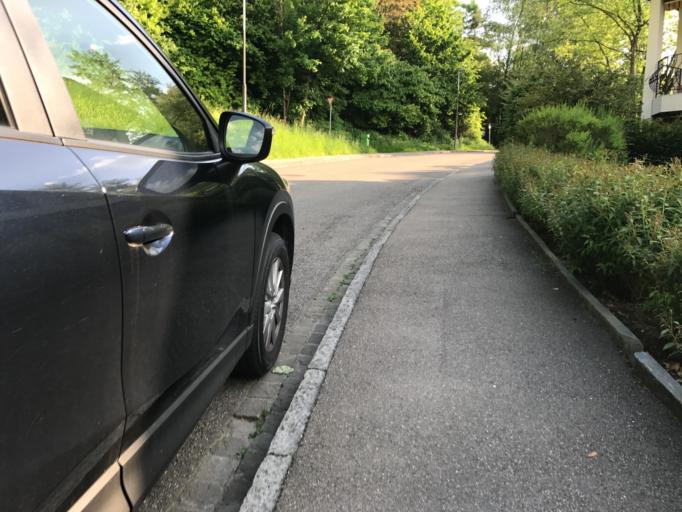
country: CH
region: Basel-City
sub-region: Basel-Stadt
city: Riehen
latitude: 47.5718
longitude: 7.6531
